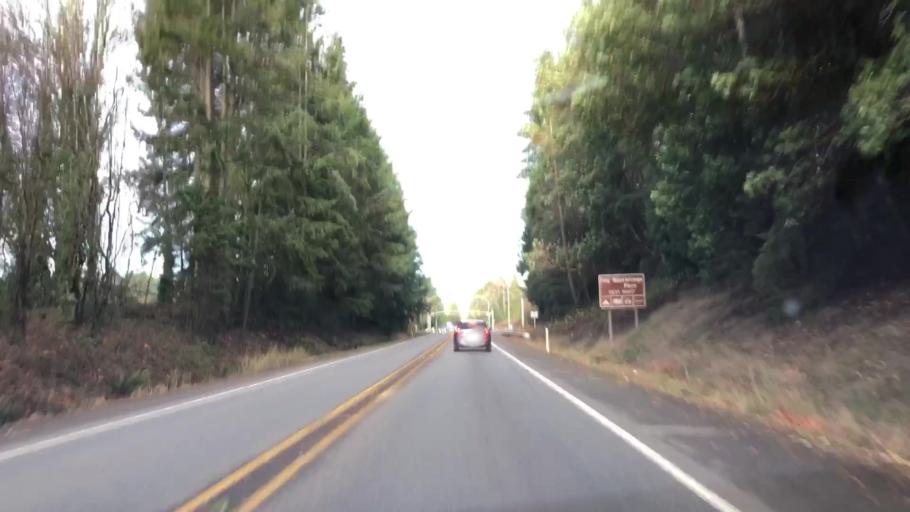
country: US
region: Washington
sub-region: Kitsap County
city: Bainbridge Island
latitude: 47.6774
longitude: -122.5372
